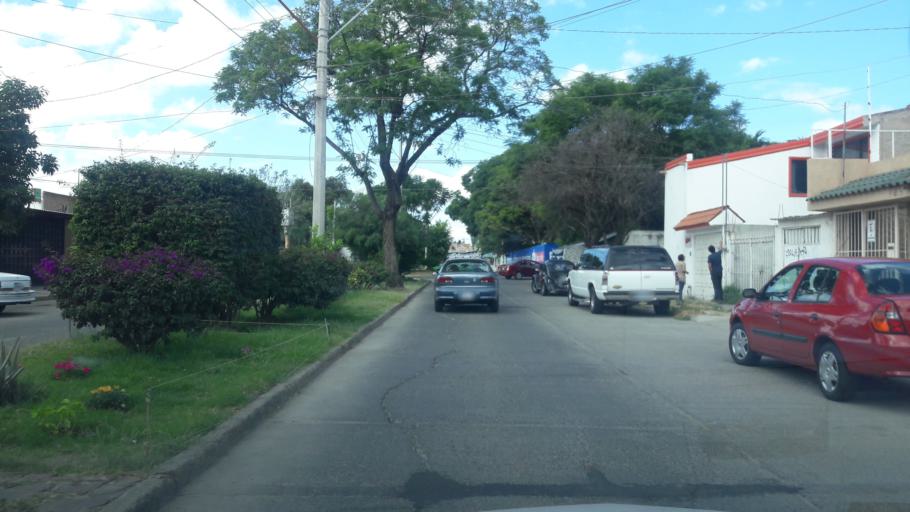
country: MX
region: Guanajuato
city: Leon
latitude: 21.1752
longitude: -101.6664
